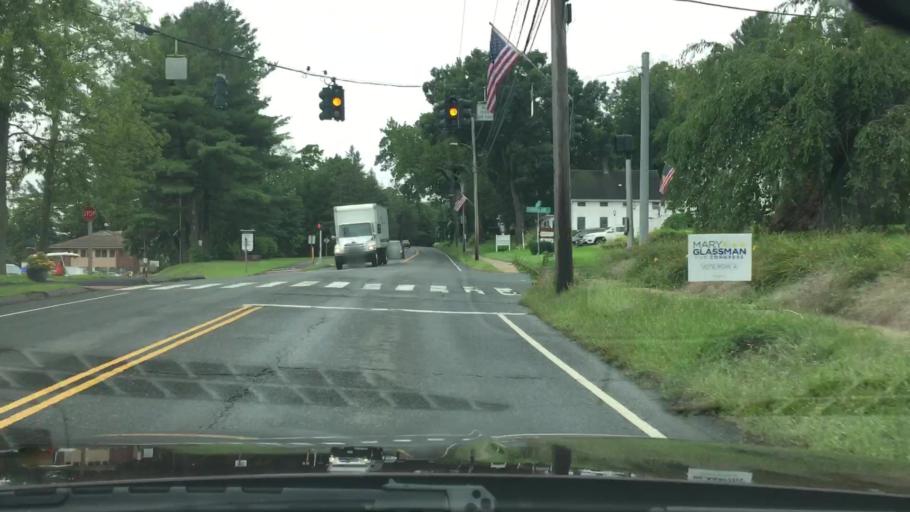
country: US
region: Connecticut
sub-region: Hartford County
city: Simsbury Center
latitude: 41.8671
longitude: -72.8066
